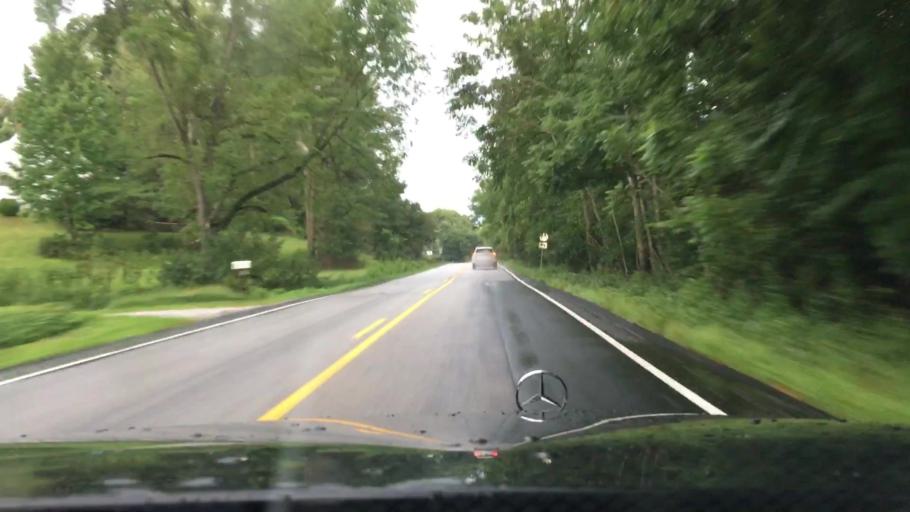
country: US
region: Virginia
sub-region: Amherst County
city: Amherst
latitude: 37.6687
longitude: -79.0125
